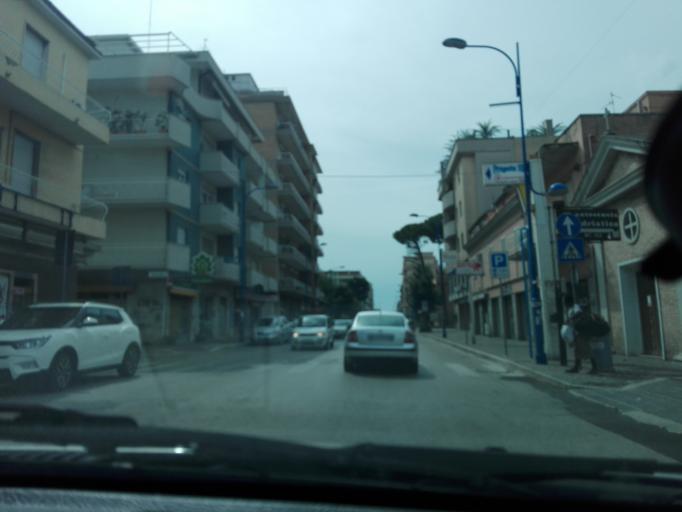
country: IT
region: Abruzzo
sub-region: Provincia di Pescara
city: Montesilvano Marina
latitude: 42.5149
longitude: 14.1517
